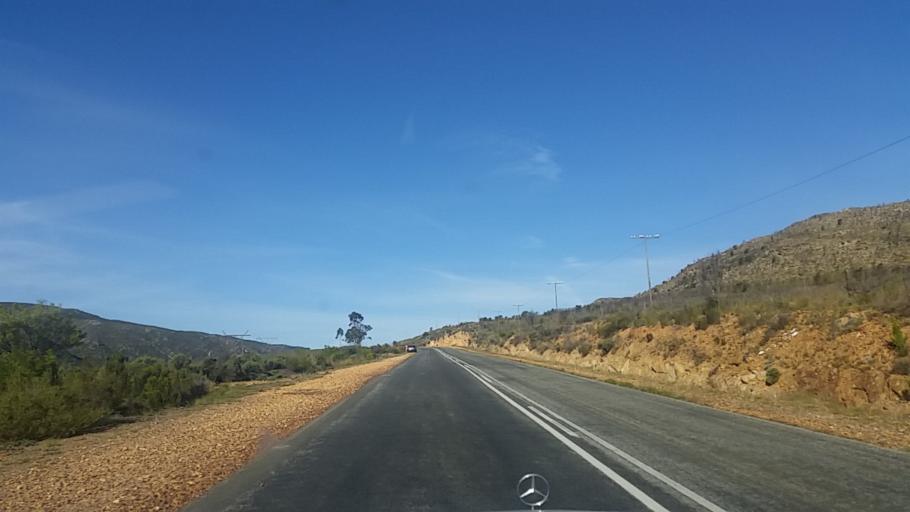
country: ZA
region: Western Cape
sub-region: Eden District Municipality
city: Knysna
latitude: -33.7533
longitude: 22.9468
